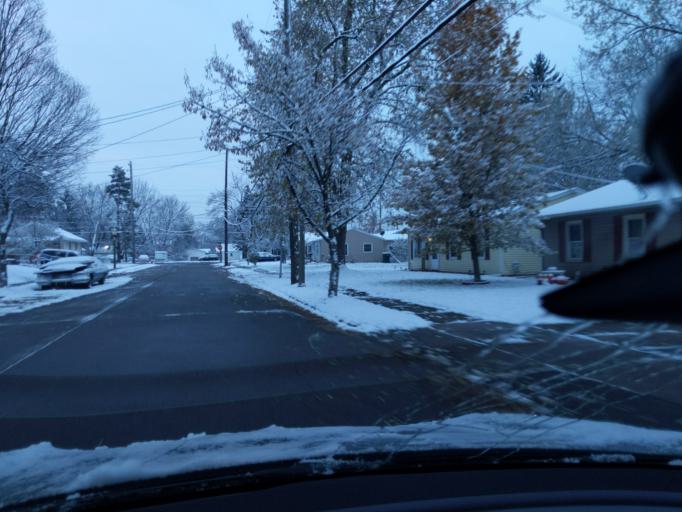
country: US
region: Michigan
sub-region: Ingham County
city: Lansing
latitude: 42.6839
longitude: -84.5587
